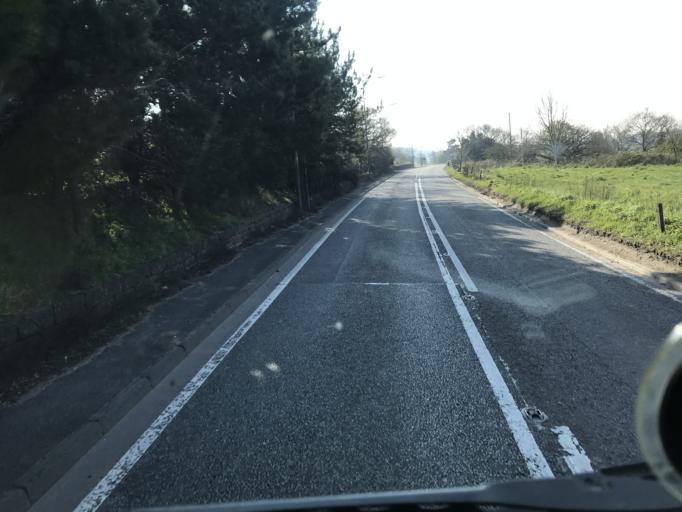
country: GB
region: England
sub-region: Cheshire West and Chester
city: Waverton
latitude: 53.1637
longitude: -2.8173
